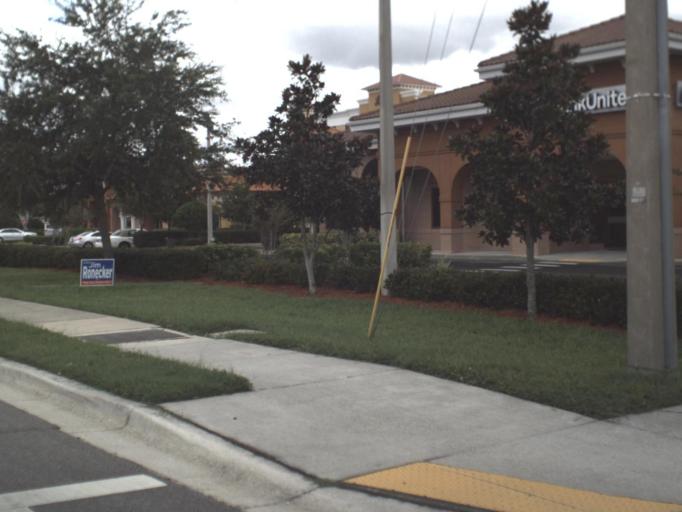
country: US
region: Florida
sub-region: Pinellas County
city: Oldsmar
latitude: 28.0366
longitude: -82.6566
